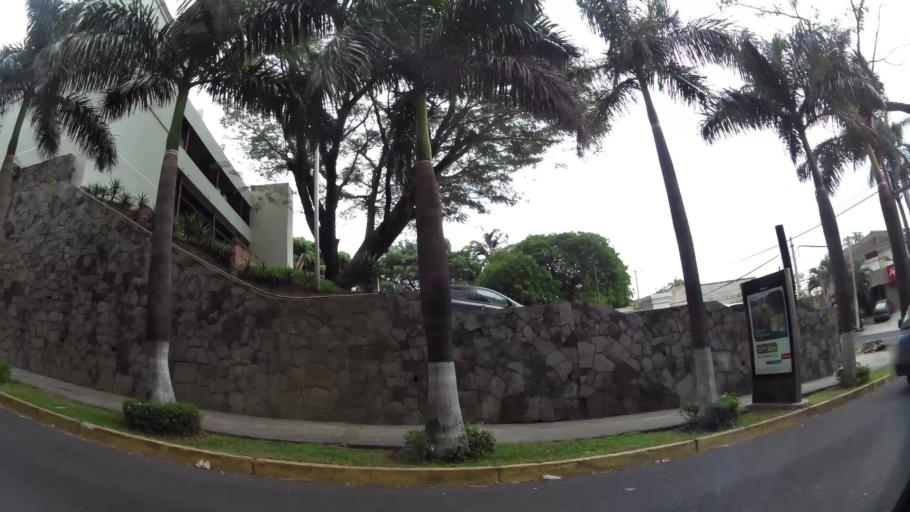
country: SV
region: San Salvador
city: Mejicanos
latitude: 13.7088
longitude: -89.2407
